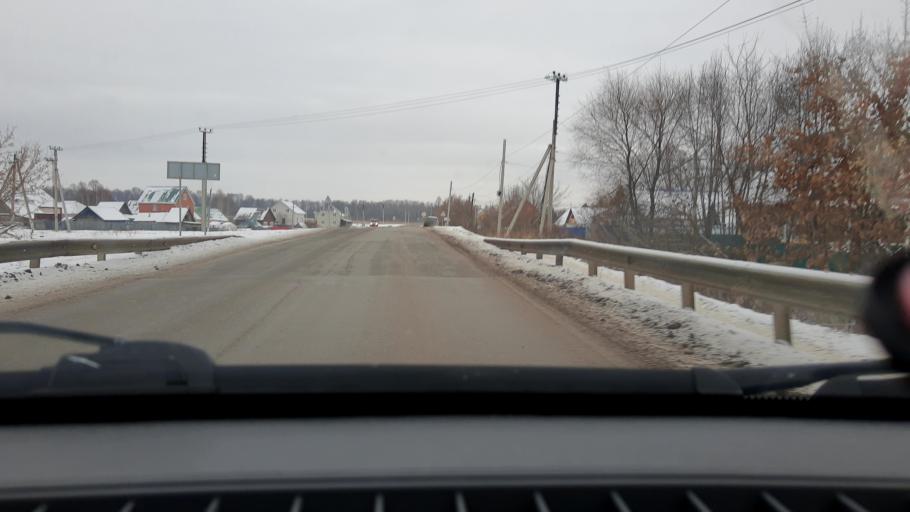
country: RU
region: Bashkortostan
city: Iglino
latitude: 54.8501
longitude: 56.4518
